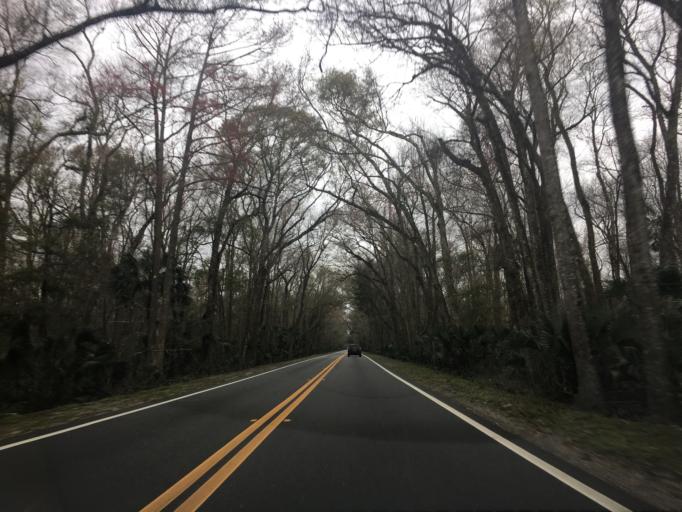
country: US
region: Florida
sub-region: Saint Johns County
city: Villano Beach
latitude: 29.9980
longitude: -81.4217
